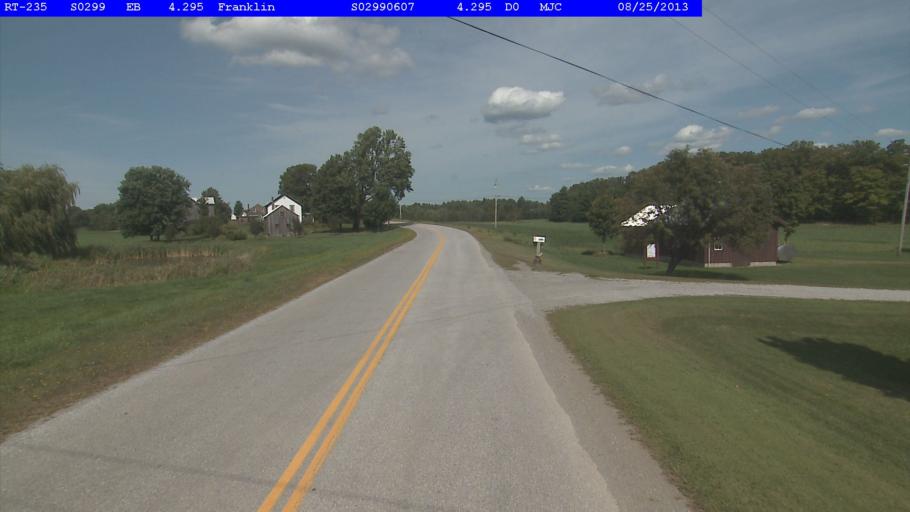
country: CA
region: Quebec
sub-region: Monteregie
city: Bedford
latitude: 45.0101
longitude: -72.9786
